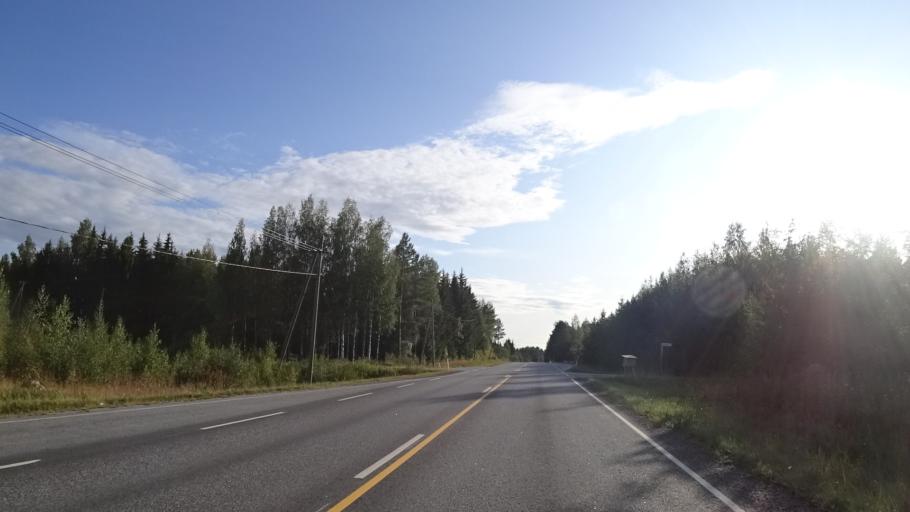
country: FI
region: South Karelia
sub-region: Imatra
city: Parikkala
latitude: 61.6130
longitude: 29.5185
